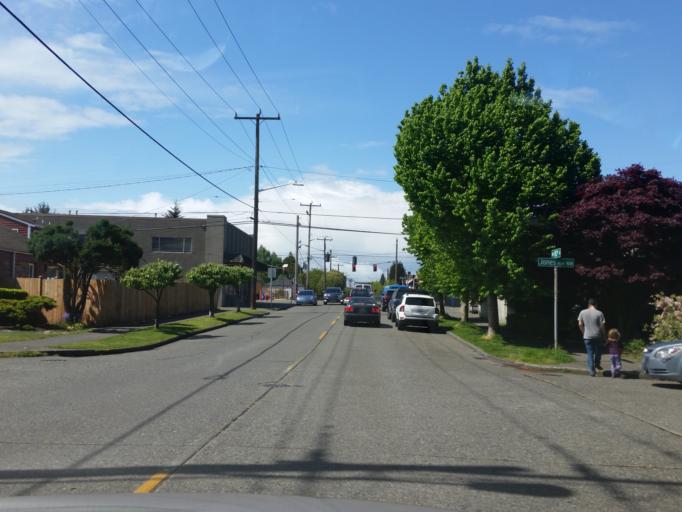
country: US
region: Washington
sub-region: King County
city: Shoreline
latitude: 47.6870
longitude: -122.3864
